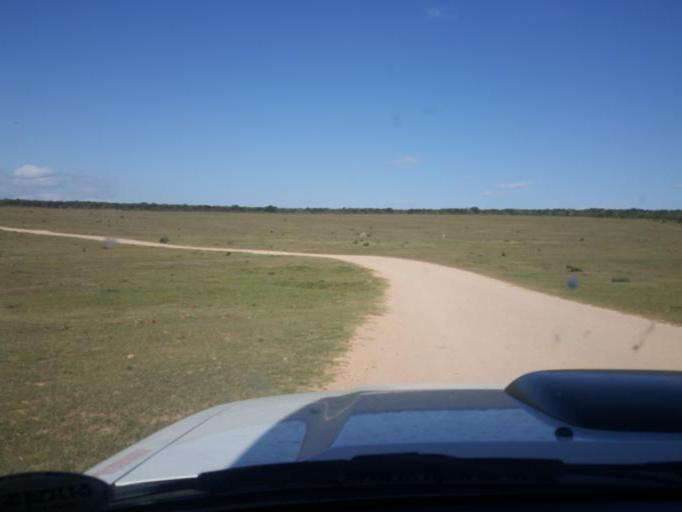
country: ZA
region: Eastern Cape
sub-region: Cacadu District Municipality
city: Kirkwood
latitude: -33.4807
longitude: 25.8264
